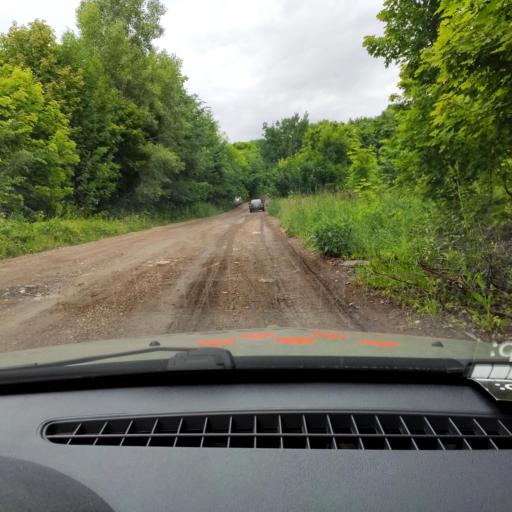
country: RU
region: Bashkortostan
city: Iglino
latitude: 54.8895
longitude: 56.2745
